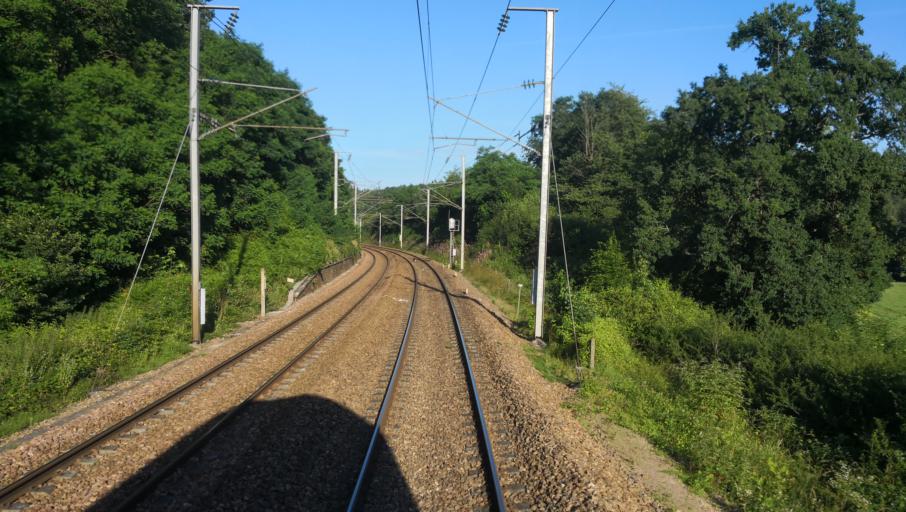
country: FR
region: Haute-Normandie
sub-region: Departement de l'Eure
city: Conches-en-Ouche
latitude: 48.9754
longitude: 0.9752
